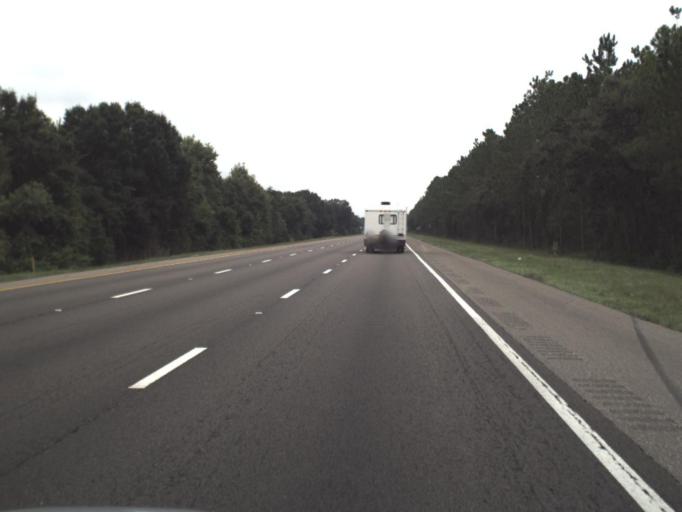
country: US
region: Florida
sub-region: Hillsborough County
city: Ruskin
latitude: 27.6459
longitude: -82.4523
